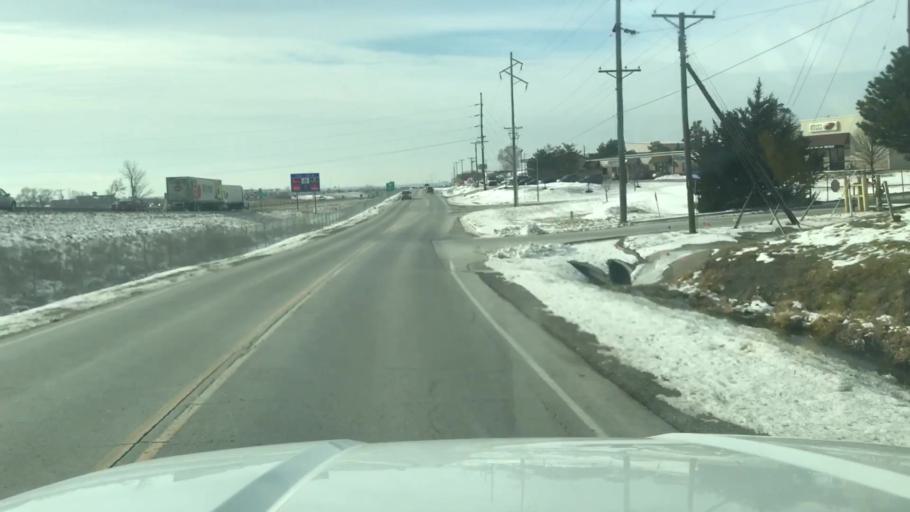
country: US
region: Missouri
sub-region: Clay County
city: Liberty
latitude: 39.2523
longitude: -94.4513
